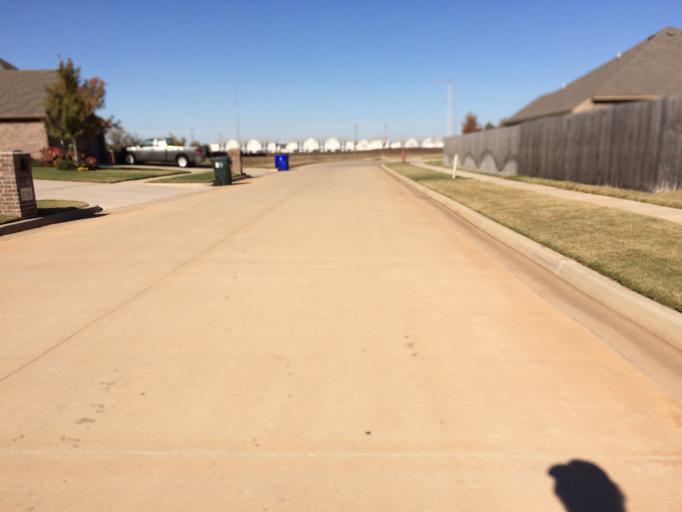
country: US
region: Oklahoma
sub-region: Cleveland County
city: Noble
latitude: 35.1730
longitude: -97.4220
